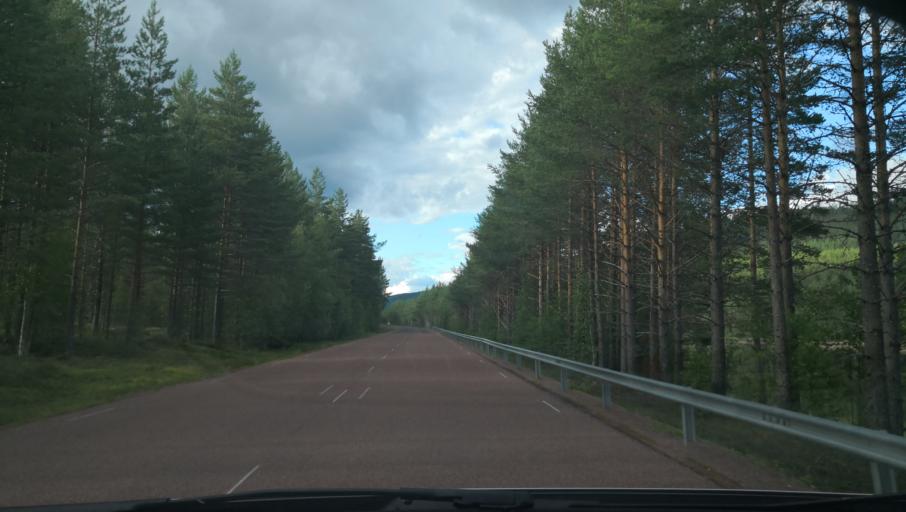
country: SE
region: Dalarna
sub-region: Alvdalens Kommun
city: AElvdalen
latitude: 61.3168
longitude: 13.7328
